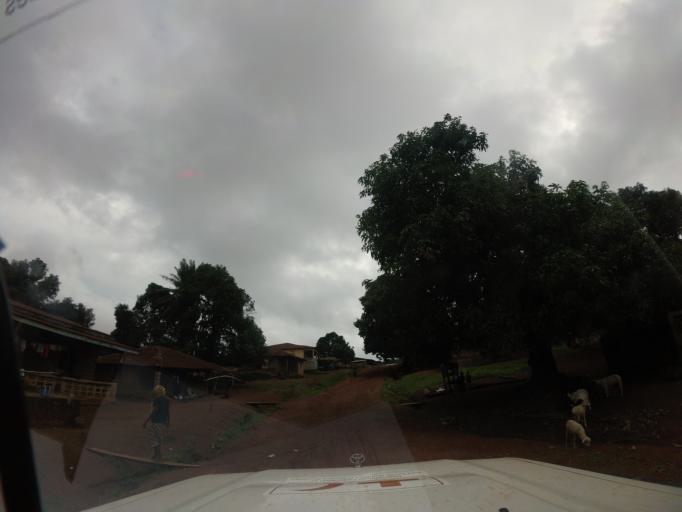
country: SL
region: Northern Province
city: Kamakwie
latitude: 9.6760
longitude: -12.2245
